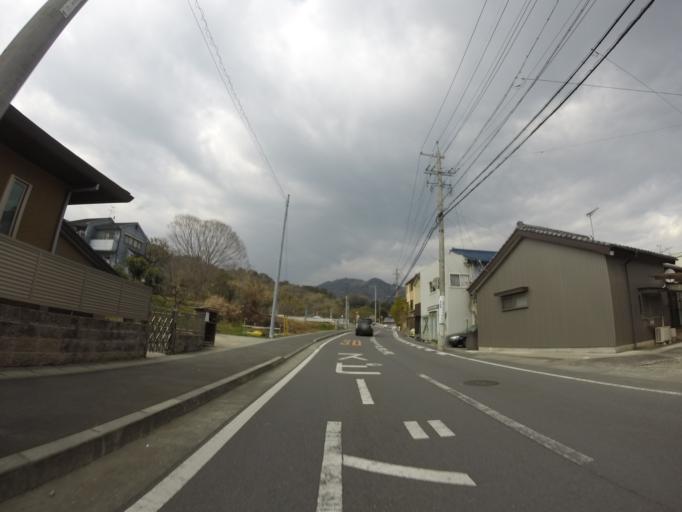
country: JP
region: Shizuoka
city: Shizuoka-shi
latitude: 35.0381
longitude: 138.4490
